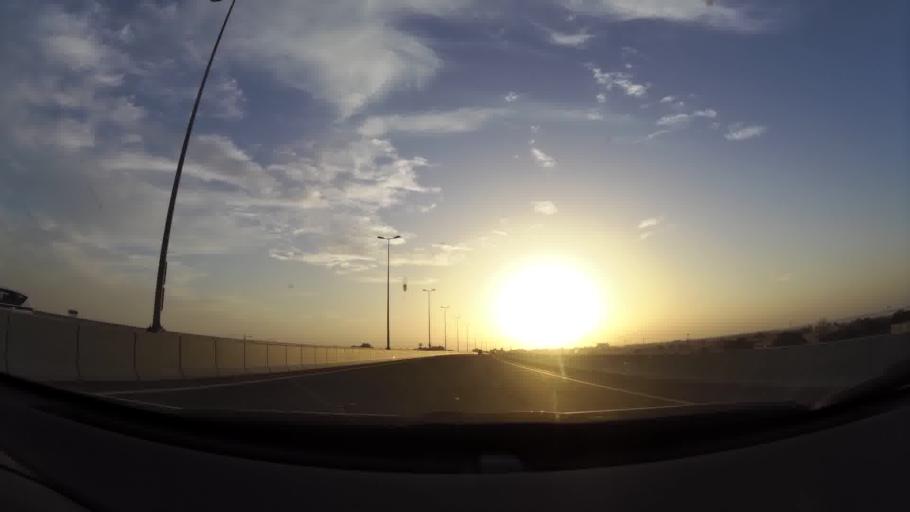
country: KW
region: Al Asimah
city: Ar Rabiyah
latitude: 29.3197
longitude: 47.8835
